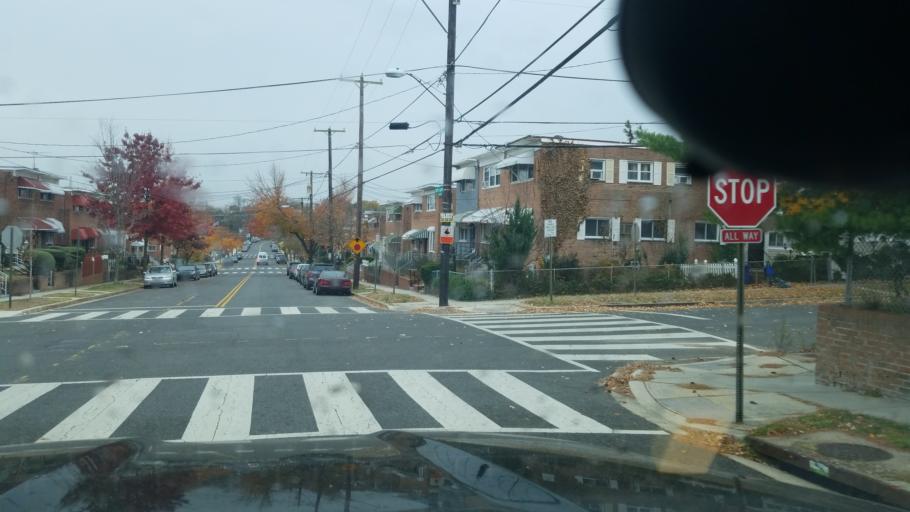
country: US
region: Maryland
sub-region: Montgomery County
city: Takoma Park
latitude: 38.9675
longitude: -77.0091
